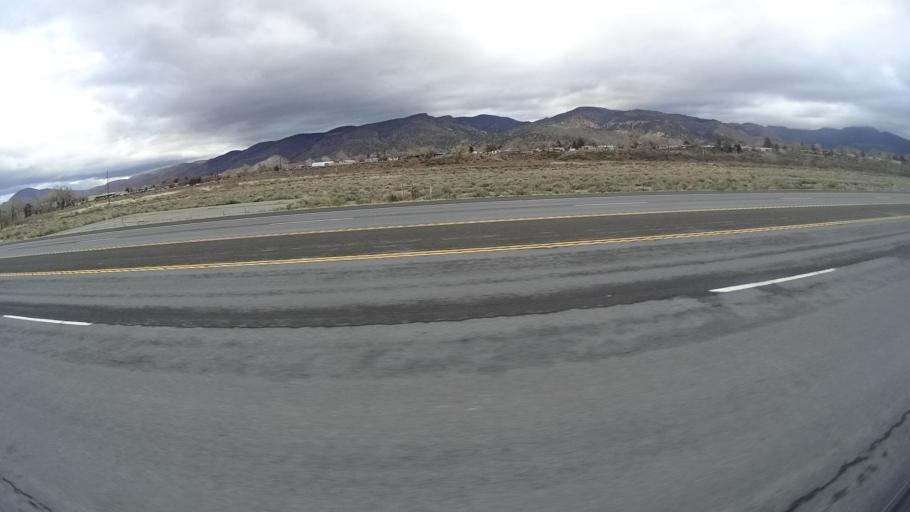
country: US
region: Nevada
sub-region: Storey County
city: Virginia City
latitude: 39.3950
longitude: -119.7428
